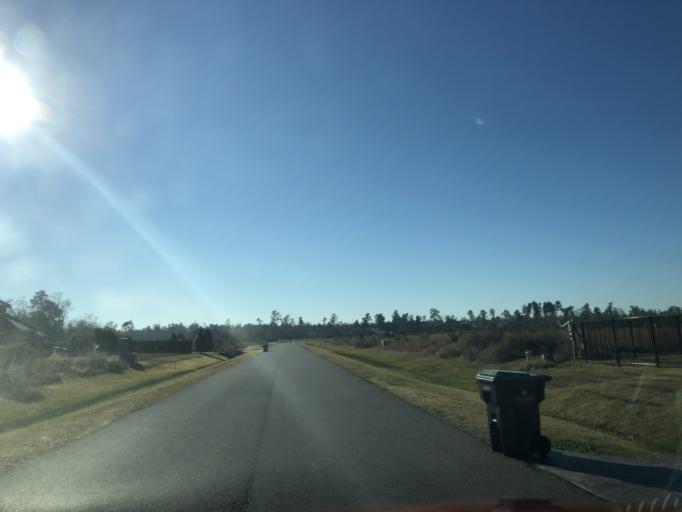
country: US
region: Texas
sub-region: Montgomery County
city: Porter Heights
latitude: 30.0762
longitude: -95.3193
